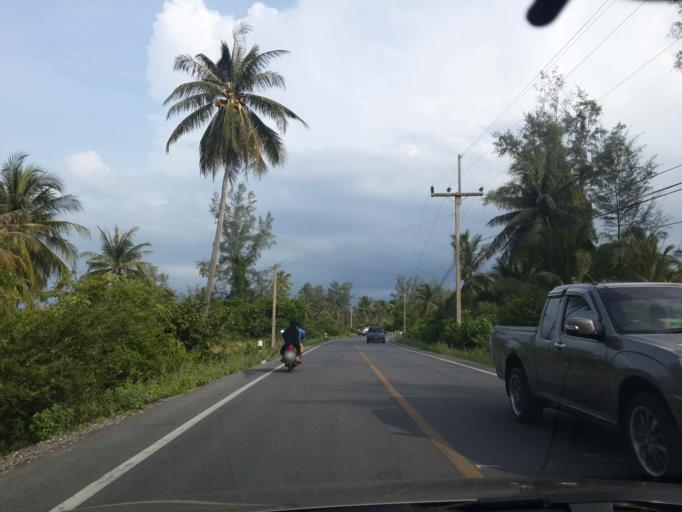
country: TH
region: Pattani
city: Yaring
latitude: 6.9016
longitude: 101.3596
